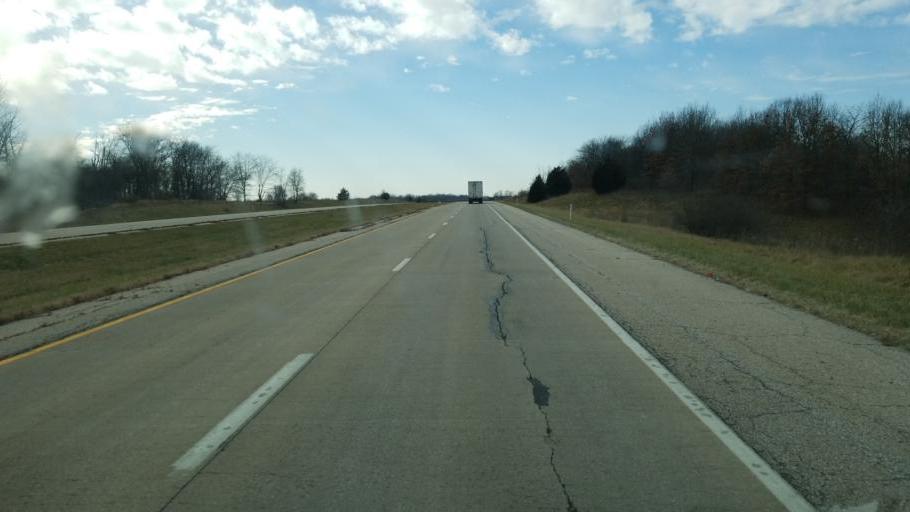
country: US
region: Illinois
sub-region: Knox County
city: Galesburg
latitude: 40.9286
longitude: -90.4310
